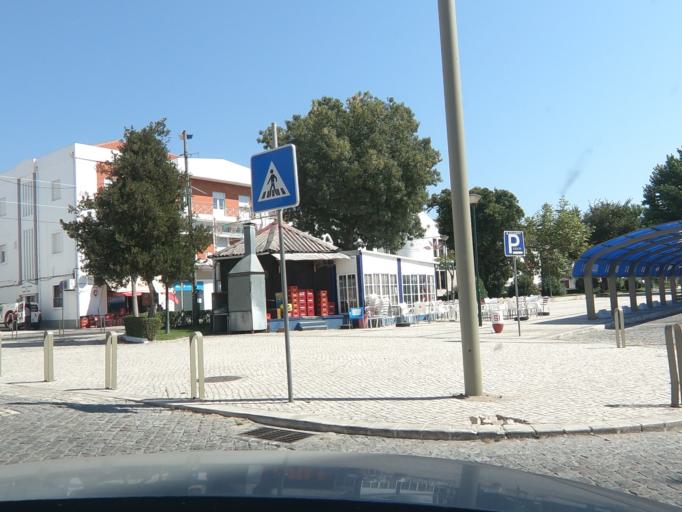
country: PT
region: Setubal
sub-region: Alcacer do Sal
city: Alcacer do Sal
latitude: 38.3696
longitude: -8.5065
